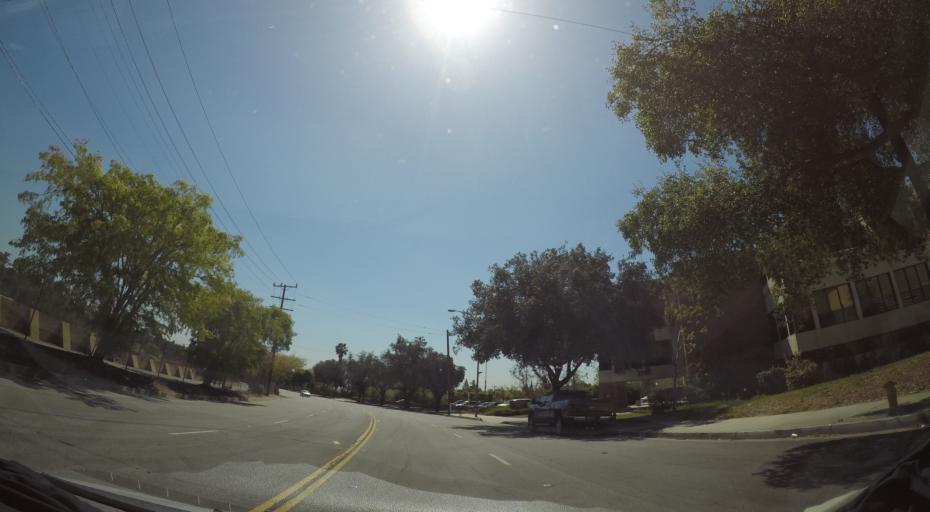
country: US
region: California
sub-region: Los Angeles County
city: East Pasadena
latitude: 34.1682
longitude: -118.0945
